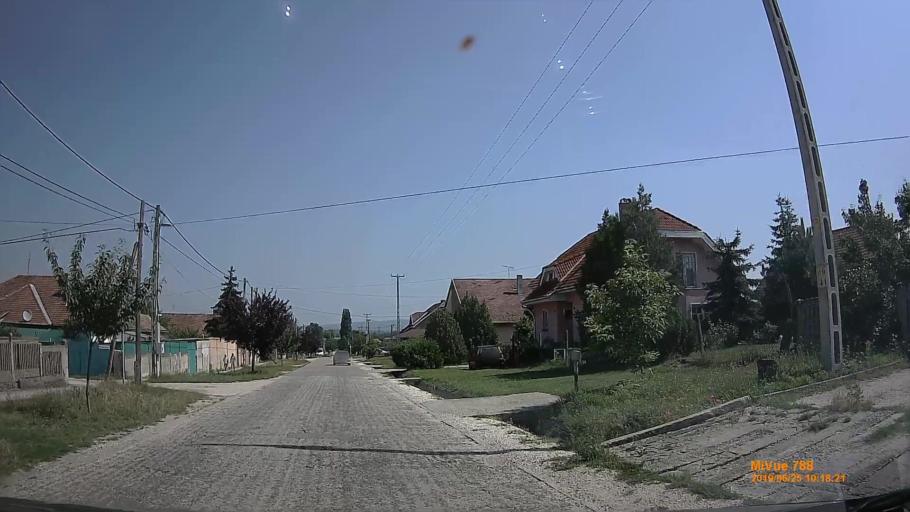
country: HU
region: Komarom-Esztergom
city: Tokod
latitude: 47.7325
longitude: 18.6926
